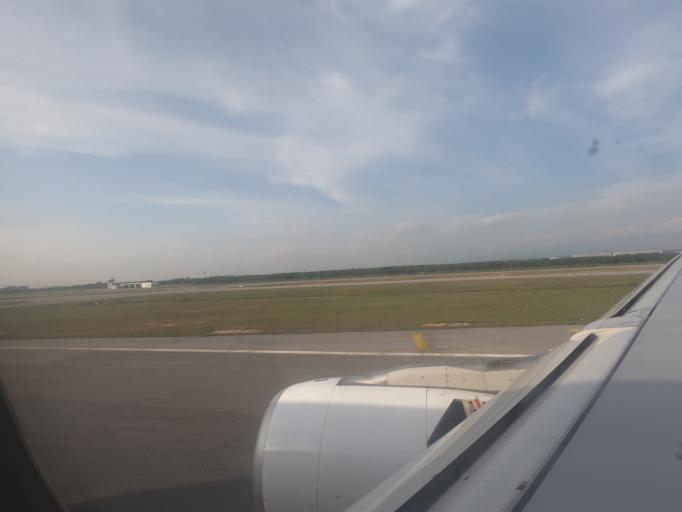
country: MY
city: Sungai Pelek New Village
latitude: 2.7190
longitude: 101.6904
